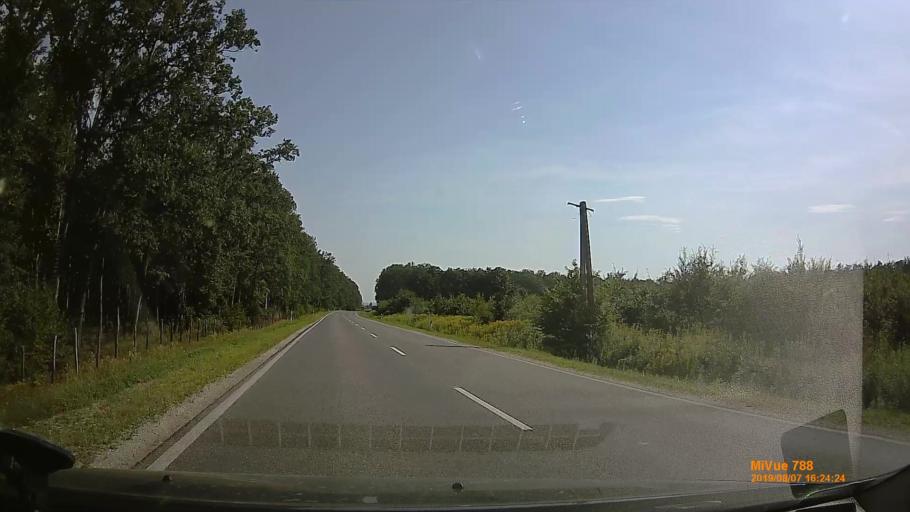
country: HU
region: Zala
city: Lenti
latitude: 46.7364
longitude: 16.5533
